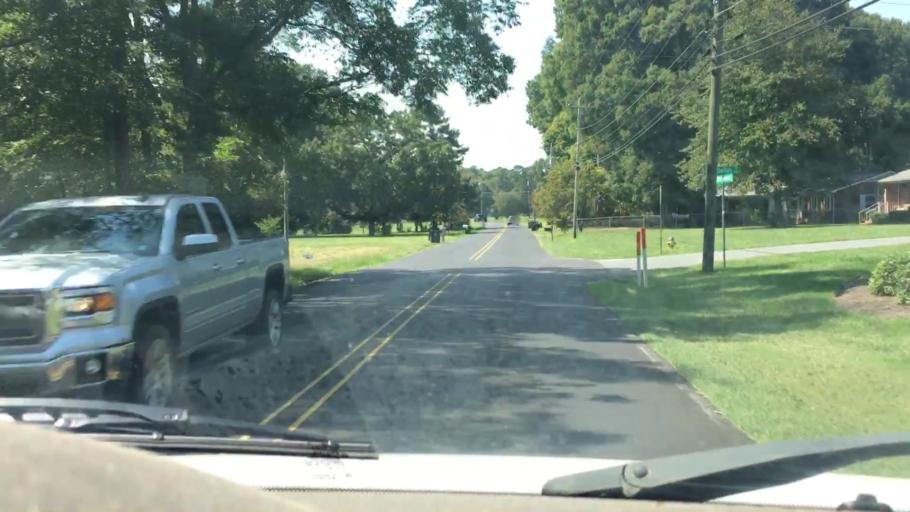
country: US
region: North Carolina
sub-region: Mecklenburg County
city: Huntersville
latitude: 35.4035
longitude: -80.8451
